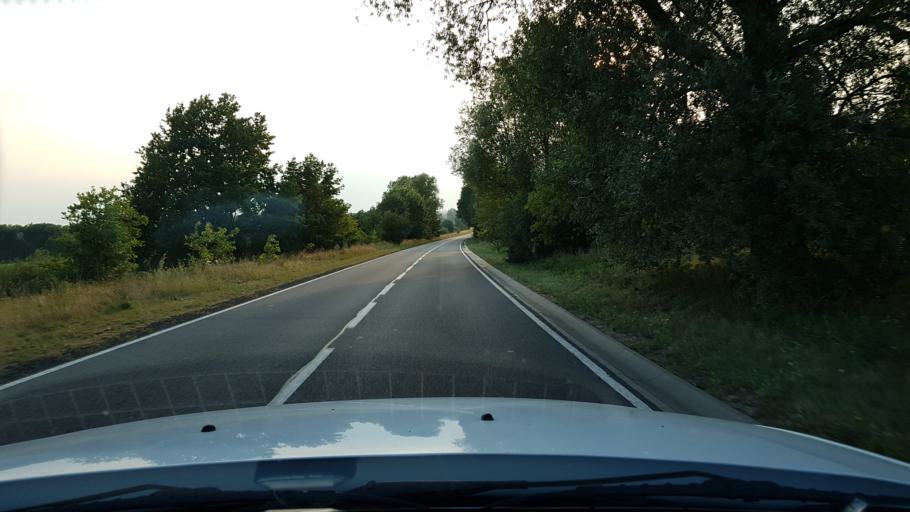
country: PL
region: West Pomeranian Voivodeship
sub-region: Powiat stargardzki
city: Marianowo
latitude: 53.4274
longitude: 15.2592
